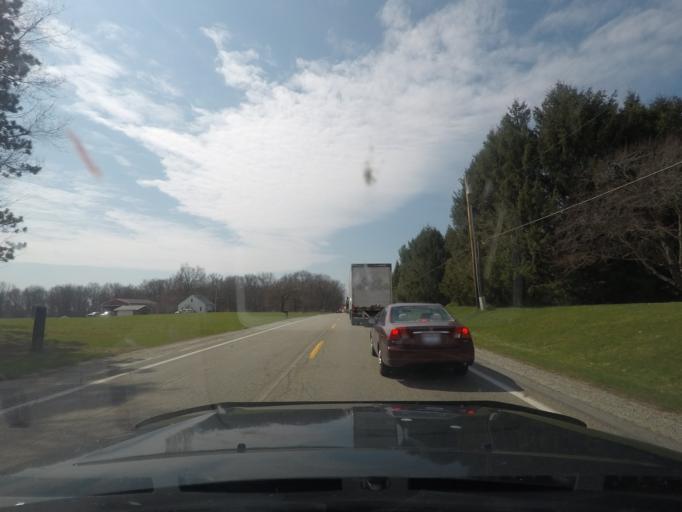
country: US
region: Indiana
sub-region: LaPorte County
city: Kingsford Heights
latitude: 41.4764
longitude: -86.6668
